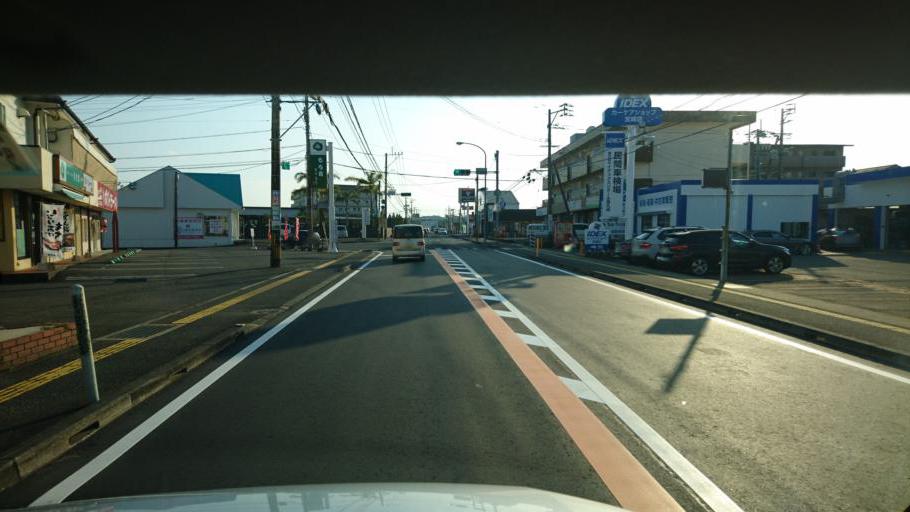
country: JP
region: Miyazaki
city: Miyazaki-shi
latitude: 31.9845
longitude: 131.4491
